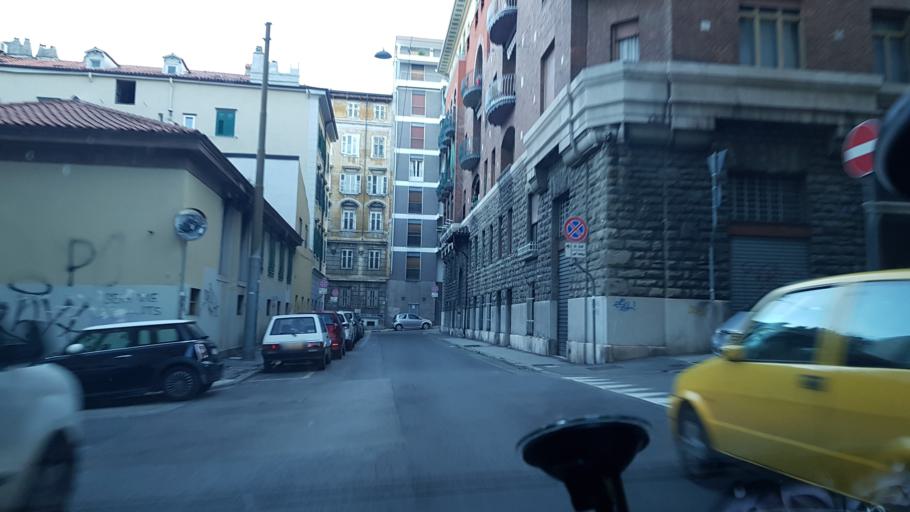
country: IT
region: Friuli Venezia Giulia
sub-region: Provincia di Trieste
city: Trieste
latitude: 45.6500
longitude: 13.7844
